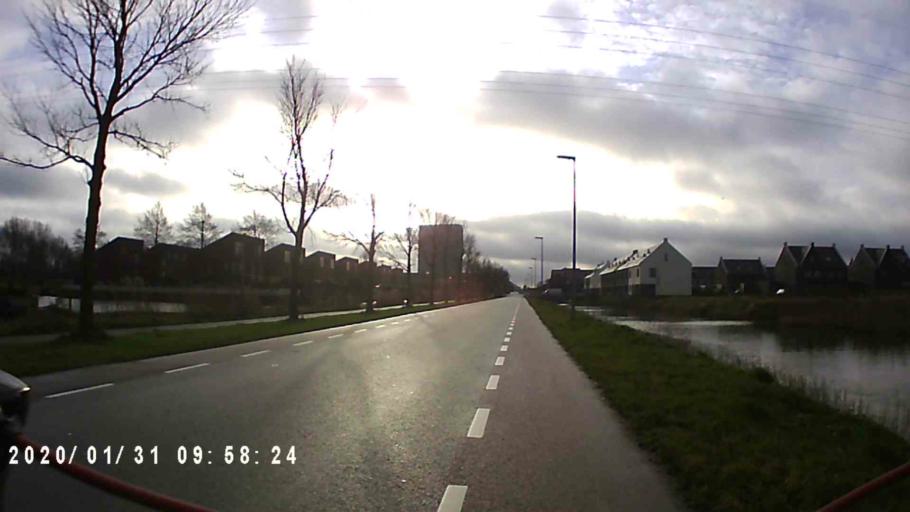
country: NL
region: Groningen
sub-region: Gemeente Groningen
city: Korrewegwijk
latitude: 53.2398
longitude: 6.5232
